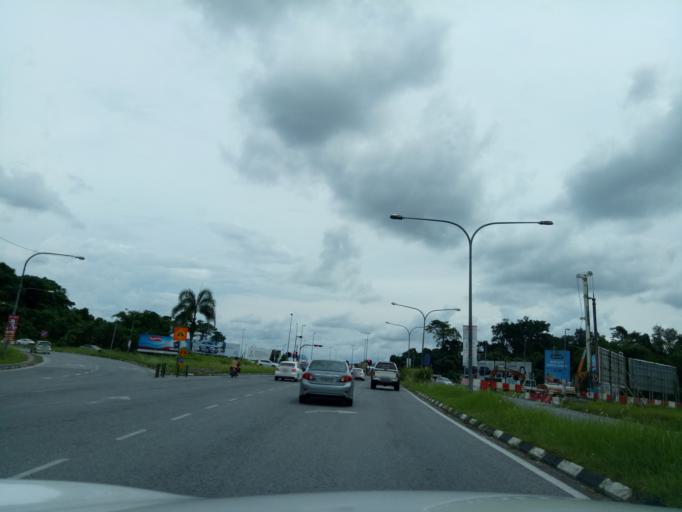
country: MY
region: Sarawak
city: Kuching
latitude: 1.4996
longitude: 110.3333
